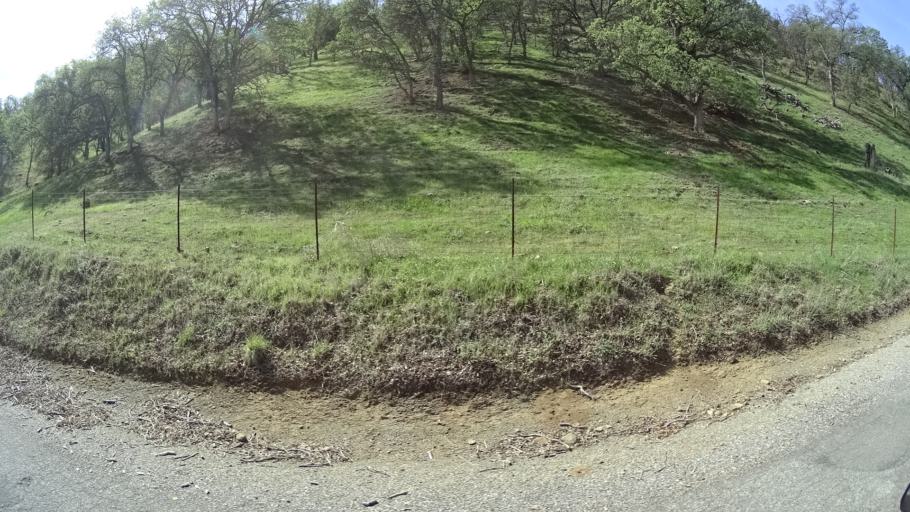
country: US
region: California
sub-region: Glenn County
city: Willows
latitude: 39.5478
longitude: -122.4008
